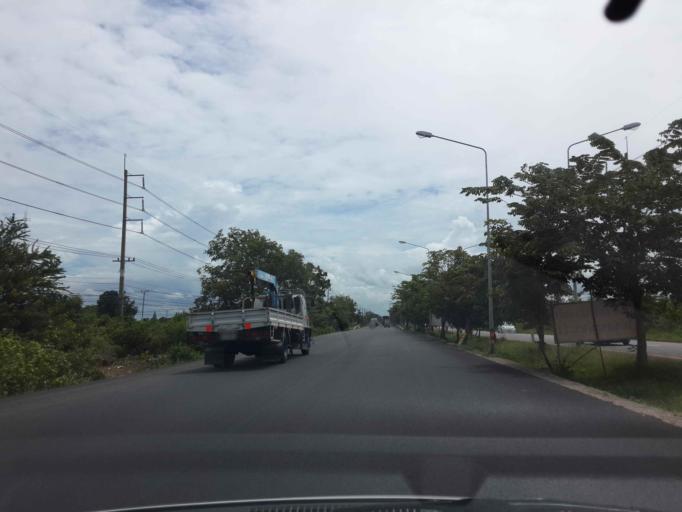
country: TH
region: Ratchaburi
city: Pak Tho
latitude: 13.4282
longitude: 99.8071
